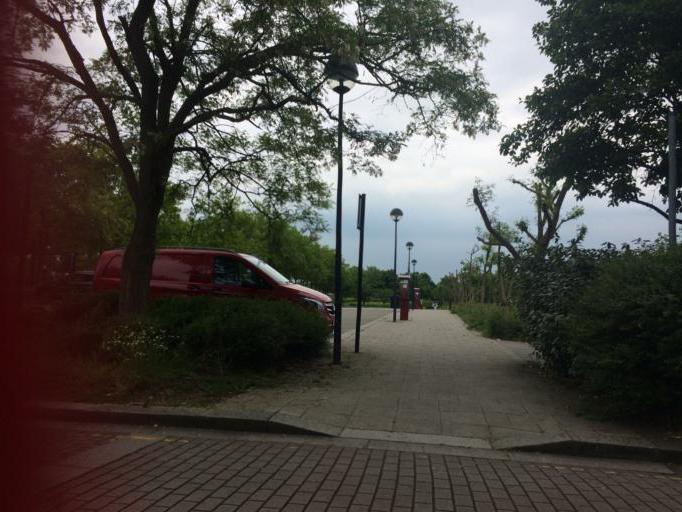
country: GB
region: England
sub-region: Milton Keynes
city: Milton Keynes
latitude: 52.0460
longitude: -0.7519
